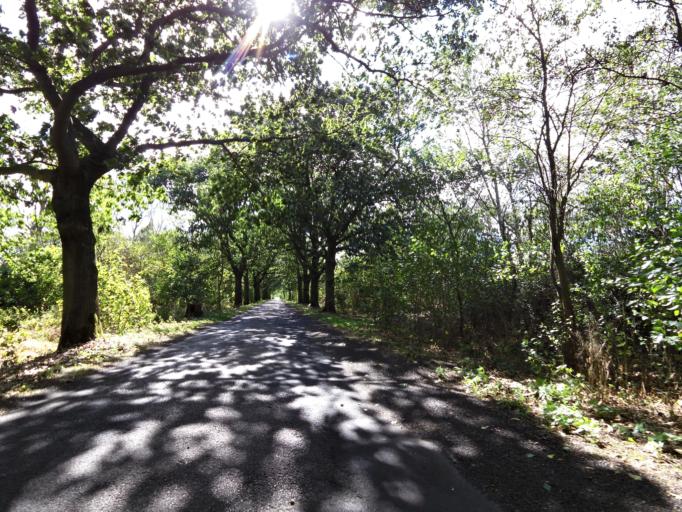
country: DE
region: Brandenburg
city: Grossbeeren
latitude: 52.3713
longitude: 13.3344
